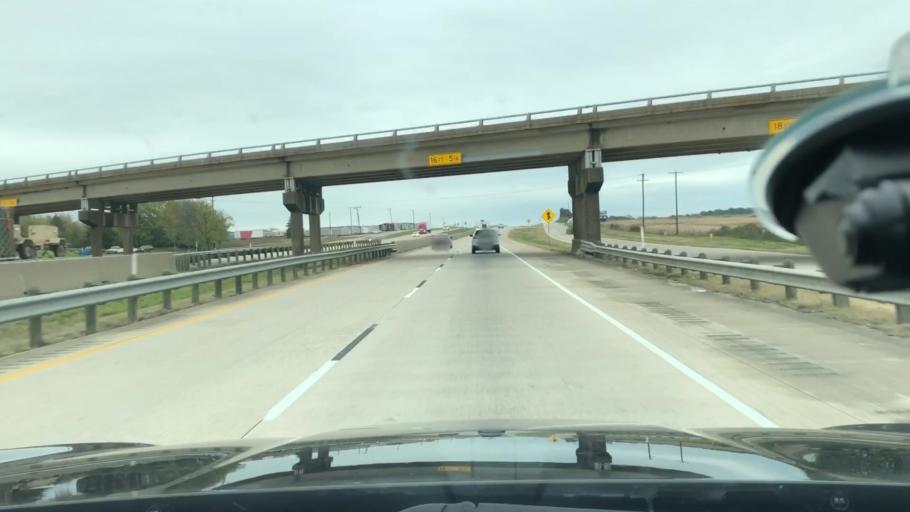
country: US
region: Texas
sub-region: Hopkins County
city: Sulphur Springs
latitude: 33.1211
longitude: -95.6722
